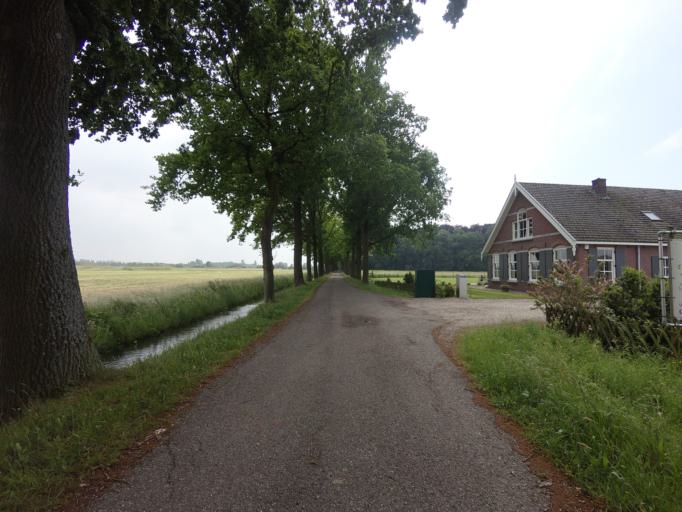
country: NL
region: Utrecht
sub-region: Stichtse Vecht
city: Spechtenkamp
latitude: 52.1158
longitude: 4.9956
